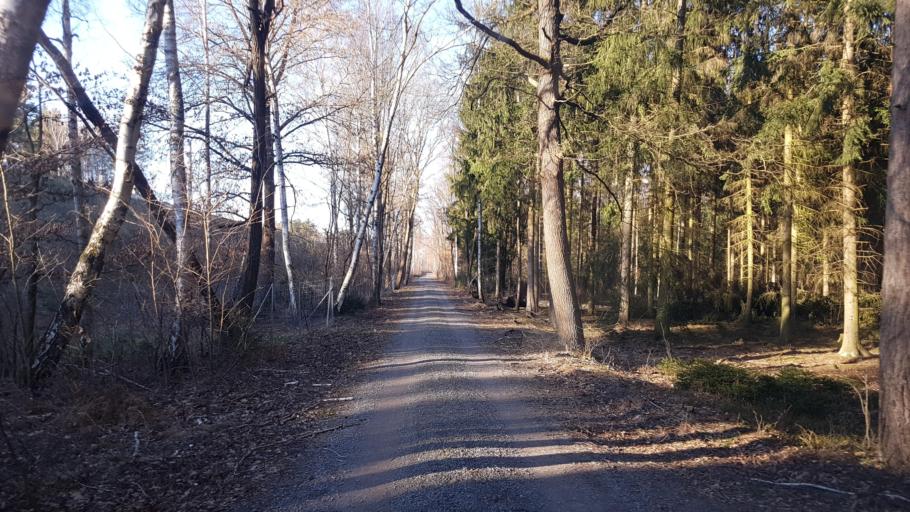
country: DE
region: Brandenburg
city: Hohenleipisch
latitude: 51.5058
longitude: 13.5769
